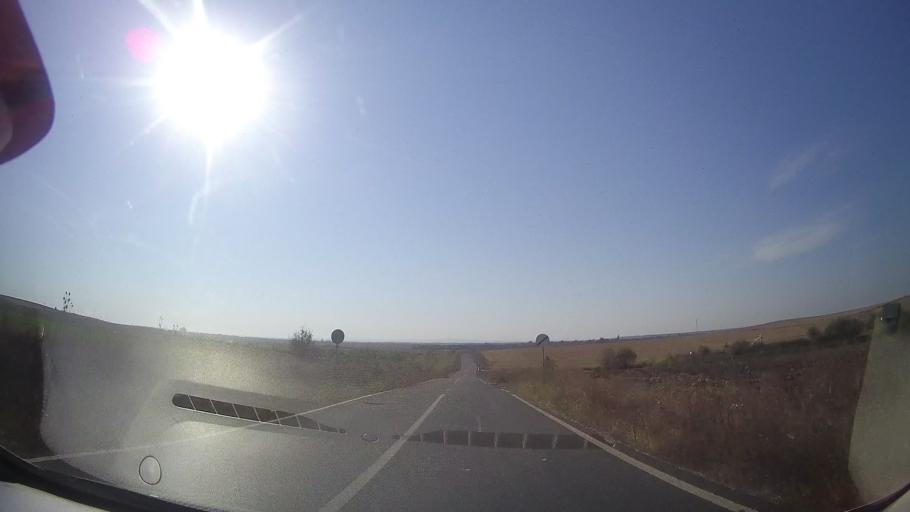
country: RO
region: Timis
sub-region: Comuna Topolovatu Mare
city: Topolovatu Mare
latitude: 45.8025
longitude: 21.5856
